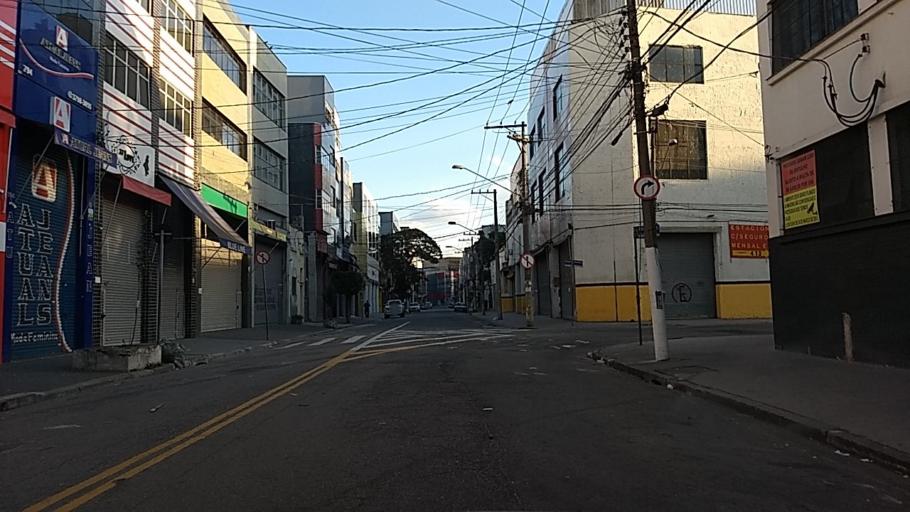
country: BR
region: Sao Paulo
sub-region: Sao Paulo
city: Sao Paulo
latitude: -23.5331
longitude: -46.6192
